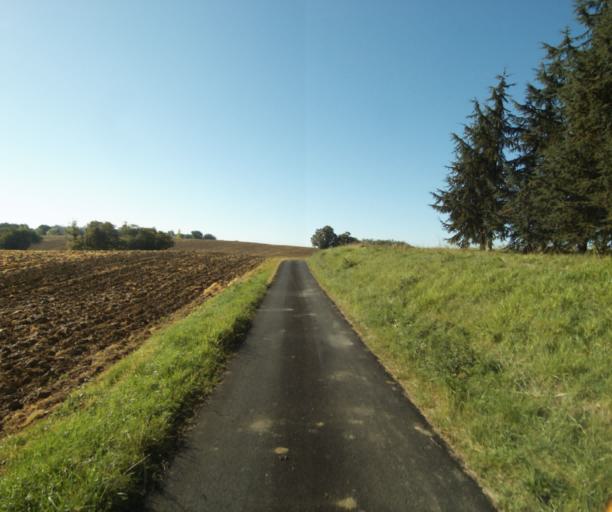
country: FR
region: Midi-Pyrenees
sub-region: Departement du Gers
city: Gondrin
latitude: 43.8300
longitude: 0.2588
